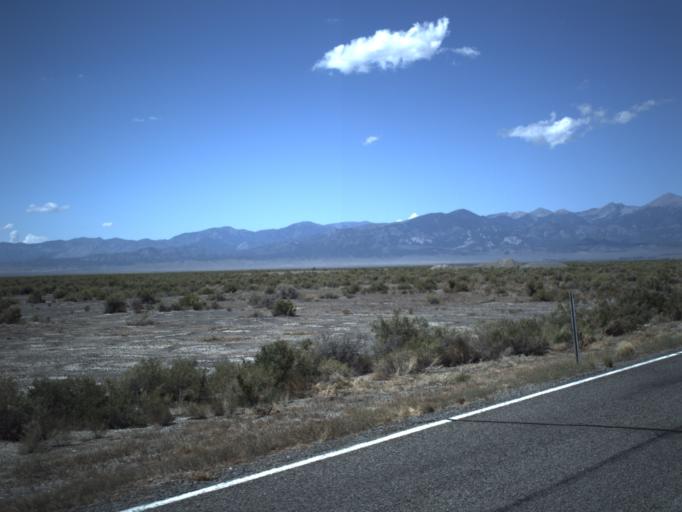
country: US
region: Nevada
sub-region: White Pine County
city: McGill
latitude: 39.0482
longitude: -113.9320
